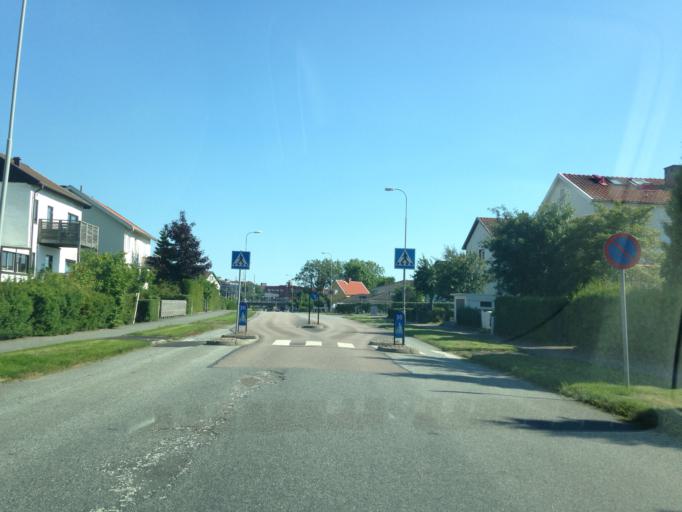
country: SE
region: Vaestra Goetaland
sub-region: Goteborg
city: Majorna
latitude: 57.7205
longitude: 11.9172
